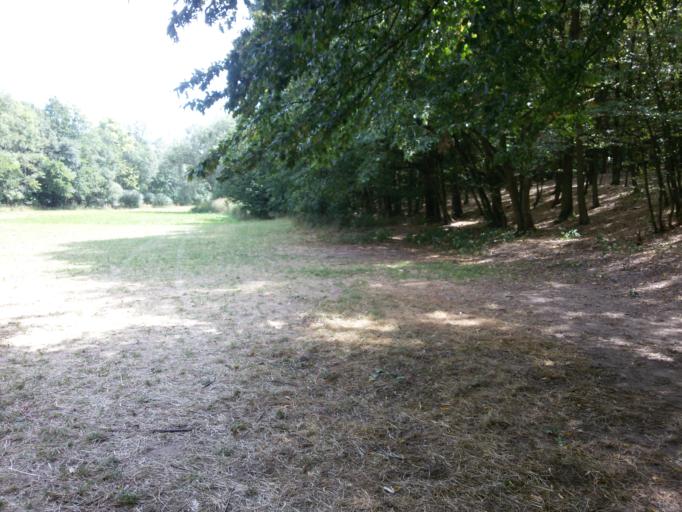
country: CZ
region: South Moravian
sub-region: Okres Znojmo
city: Jevisovice
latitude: 49.0310
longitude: 15.9909
